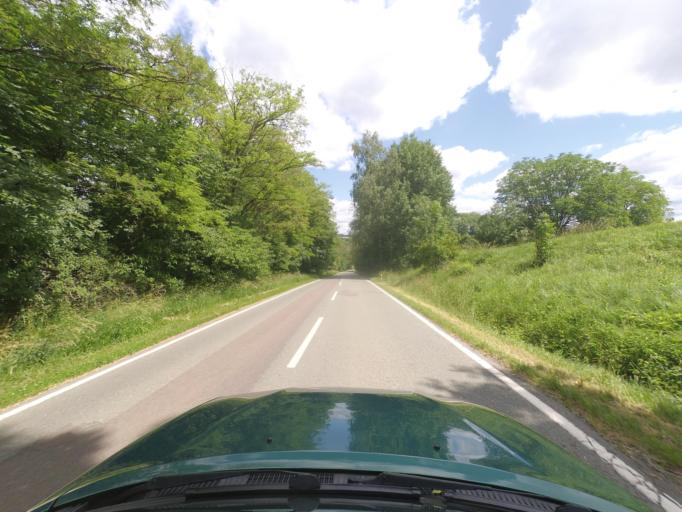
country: CZ
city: Dobruska
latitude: 50.3214
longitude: 16.2042
